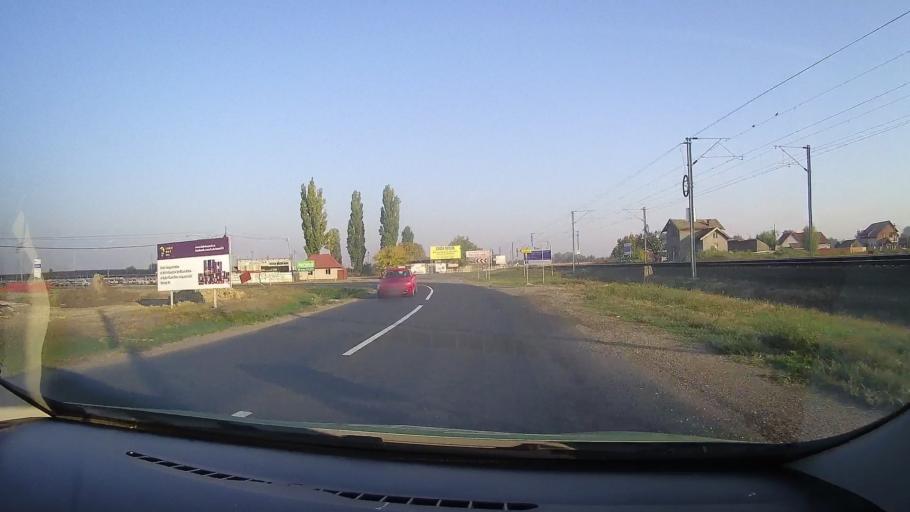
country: RO
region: Arad
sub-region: Comuna Curtici
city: Curtici
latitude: 46.3294
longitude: 21.3049
